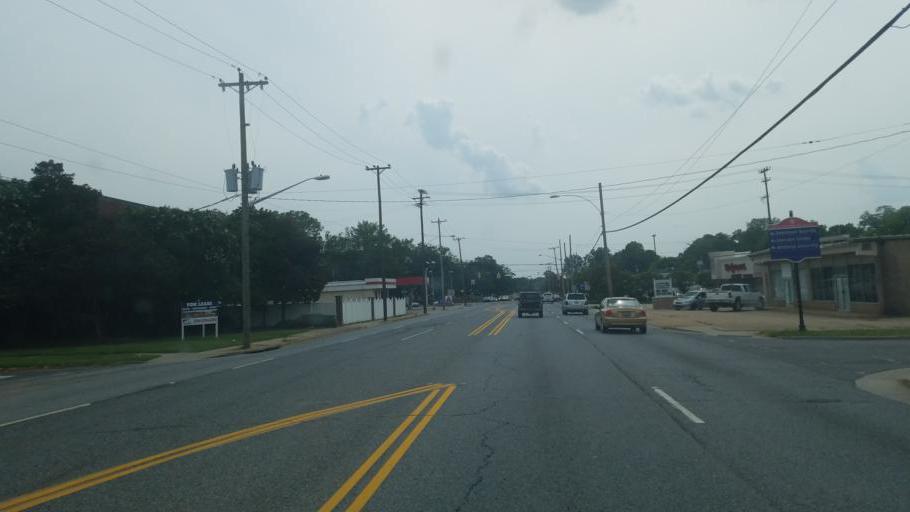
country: US
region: South Carolina
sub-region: York County
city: Rock Hill
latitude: 34.9439
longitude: -81.0295
